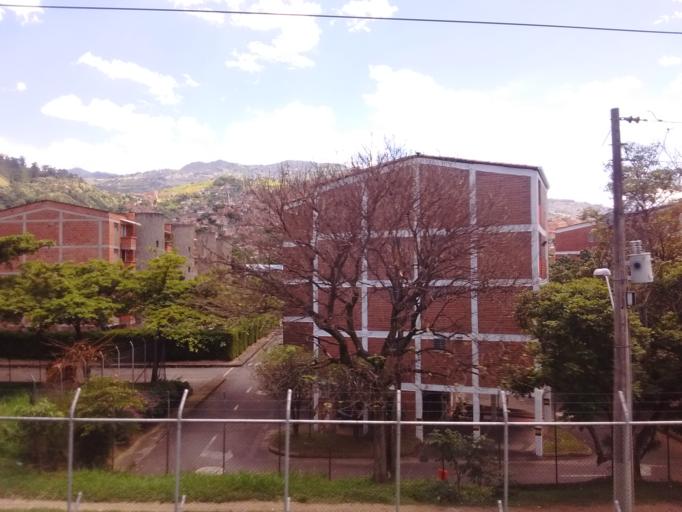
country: CO
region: Antioquia
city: Medellin
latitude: 6.2560
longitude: -75.6110
